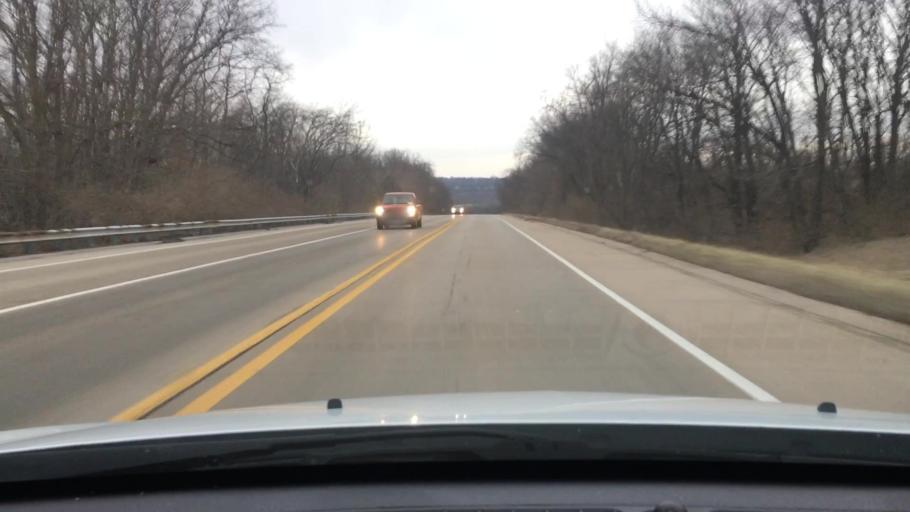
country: US
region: Illinois
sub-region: LaSalle County
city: Peru
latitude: 41.3045
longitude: -89.1102
